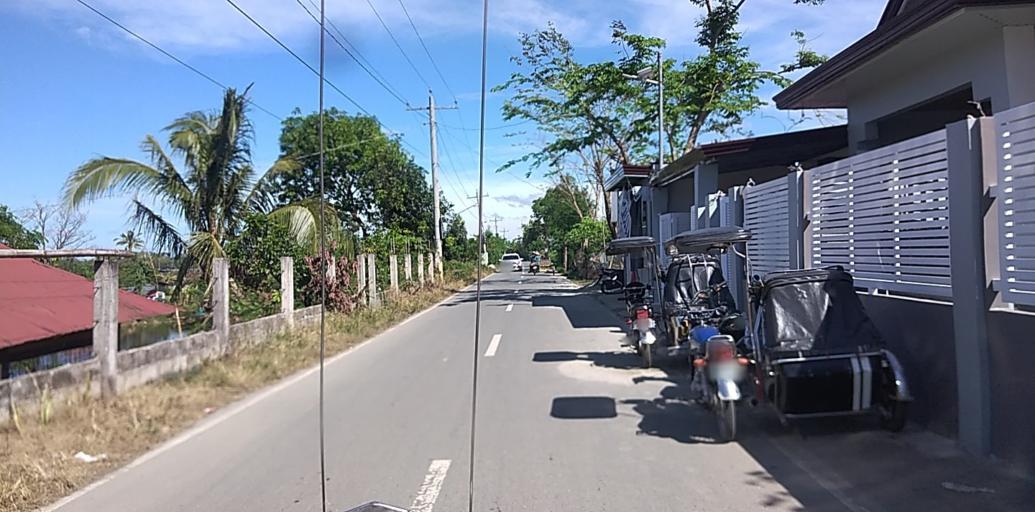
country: PH
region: Central Luzon
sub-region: Province of Pampanga
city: Candaba
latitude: 15.1070
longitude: 120.8162
